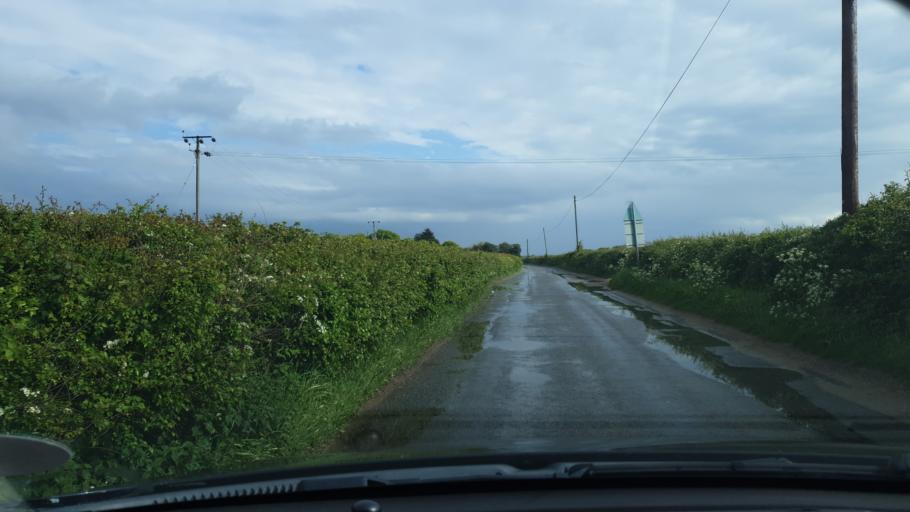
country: GB
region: England
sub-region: Essex
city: Great Bentley
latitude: 51.8485
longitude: 1.0458
